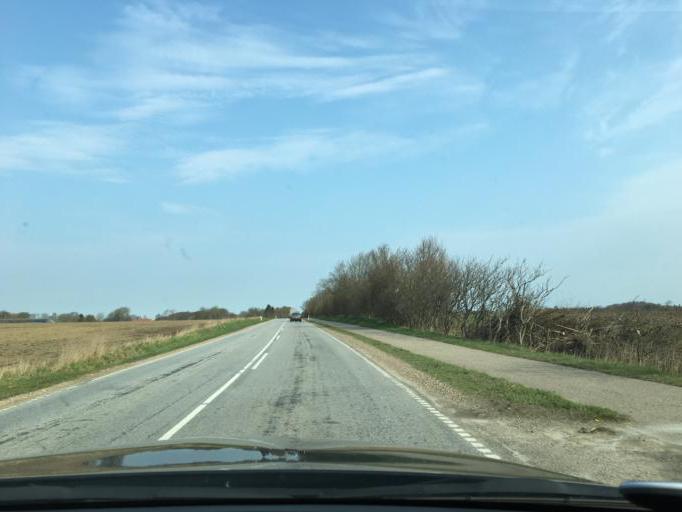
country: DK
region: South Denmark
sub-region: Esbjerg Kommune
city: Bramming
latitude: 55.4888
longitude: 8.7014
